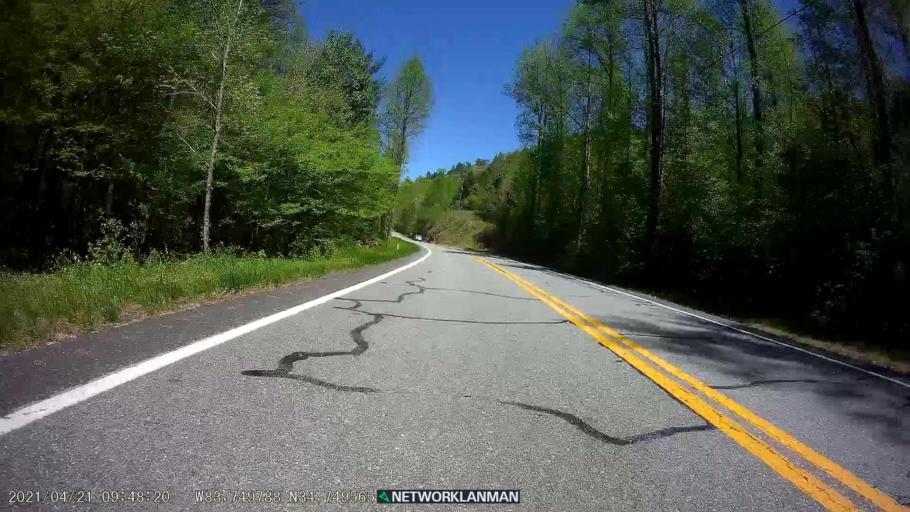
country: US
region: Georgia
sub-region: White County
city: Cleveland
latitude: 34.7495
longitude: -83.7498
